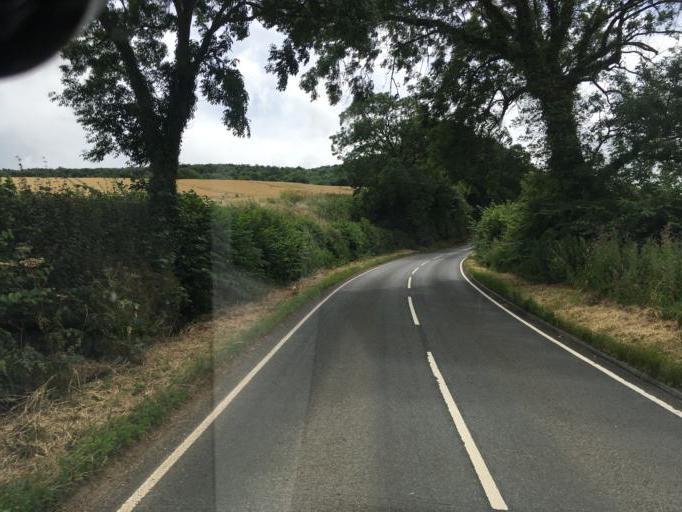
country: GB
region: England
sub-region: Gloucestershire
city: Stonehouse
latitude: 51.7187
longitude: -2.3039
